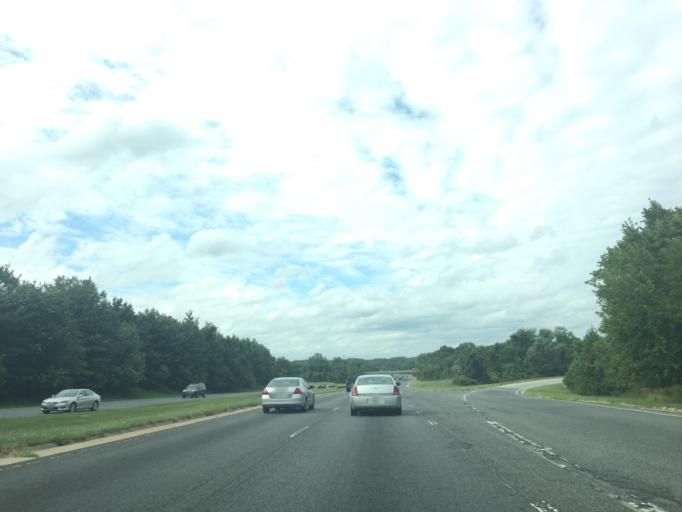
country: US
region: Maryland
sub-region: Howard County
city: Fort George G Mead Junction
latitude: 39.1173
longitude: -76.7735
